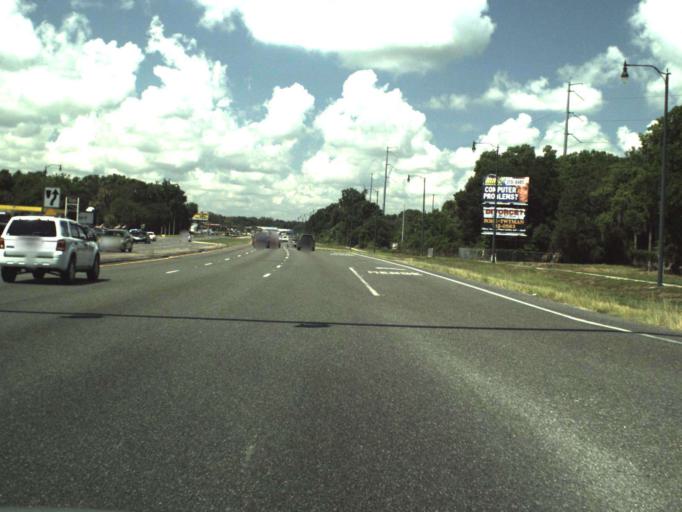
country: US
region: Florida
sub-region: Lake County
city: Silver Lake
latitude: 28.8252
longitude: -81.8316
